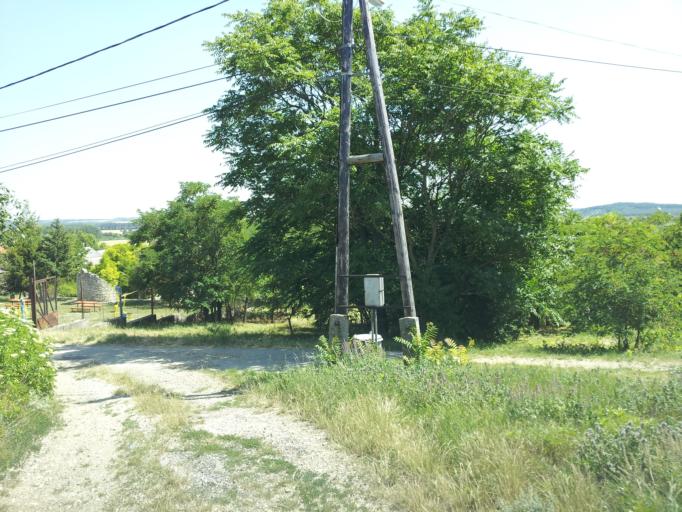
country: HU
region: Veszprem
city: Liter
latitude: 47.1101
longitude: 18.0433
